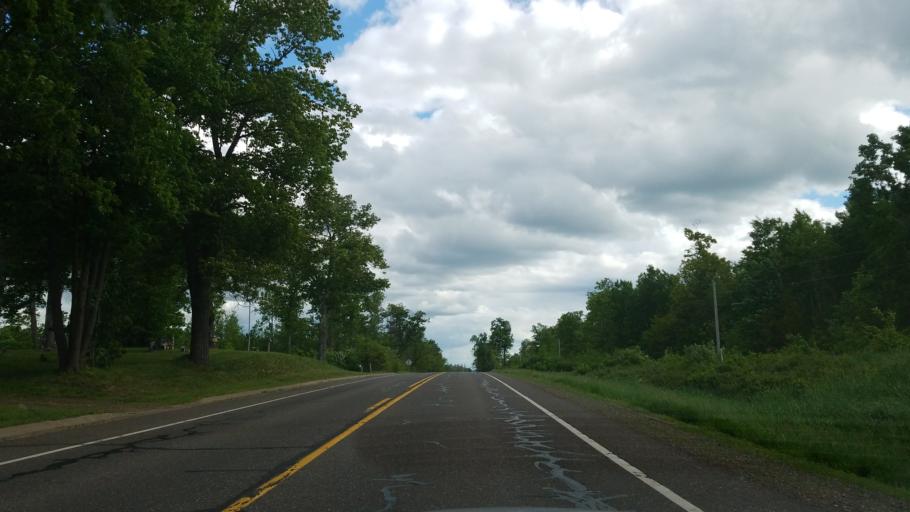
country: US
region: Wisconsin
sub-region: Burnett County
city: Siren
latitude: 46.1176
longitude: -92.2377
